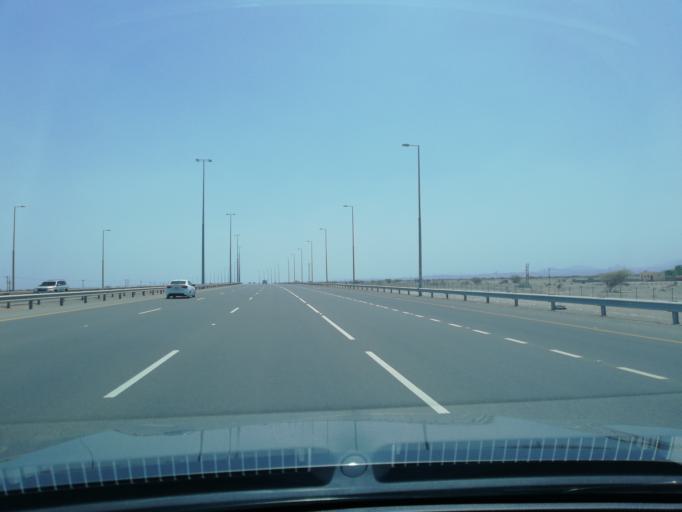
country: OM
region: Al Batinah
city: Barka'
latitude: 23.6186
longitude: 57.9116
